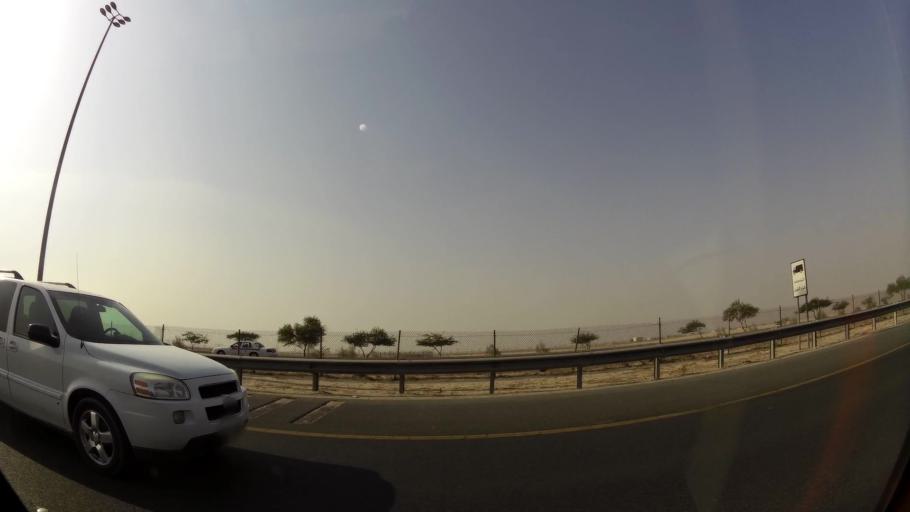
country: KW
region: Mubarak al Kabir
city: Mubarak al Kabir
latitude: 29.1753
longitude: 48.0368
